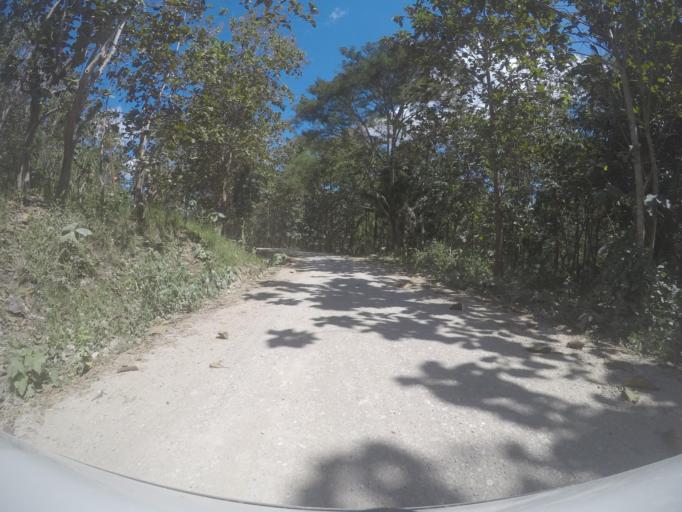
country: TL
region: Viqueque
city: Viqueque
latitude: -8.9072
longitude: 126.3927
